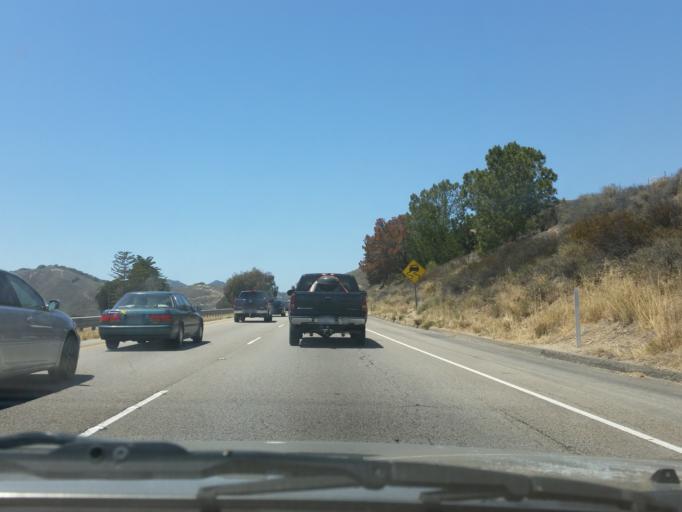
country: US
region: California
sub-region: San Luis Obispo County
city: Avila Beach
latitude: 35.1676
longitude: -120.6903
